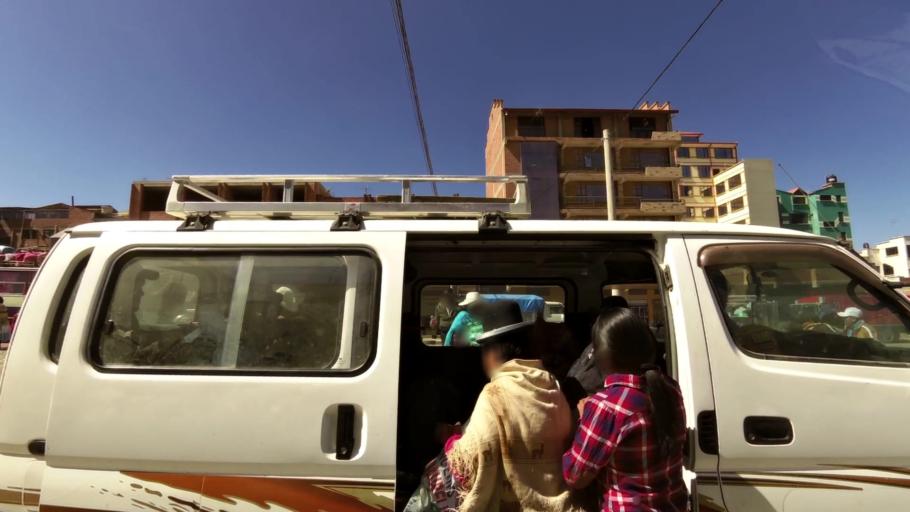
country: BO
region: La Paz
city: La Paz
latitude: -16.5347
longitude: -68.1921
